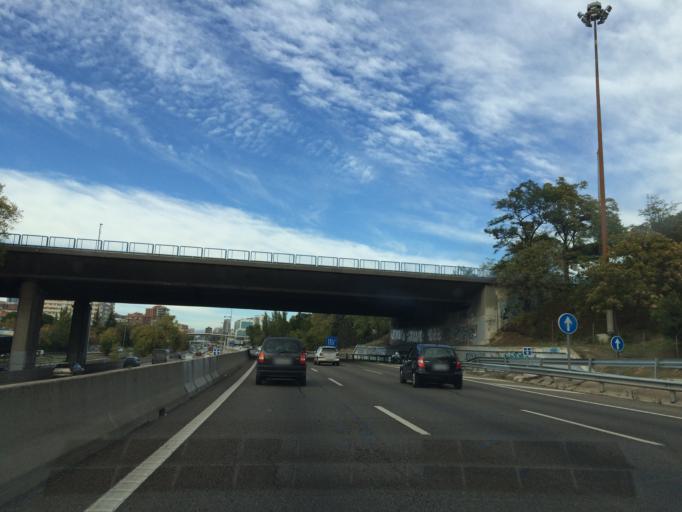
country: ES
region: Madrid
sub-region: Provincia de Madrid
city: Chamartin
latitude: 40.4595
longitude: -3.6642
